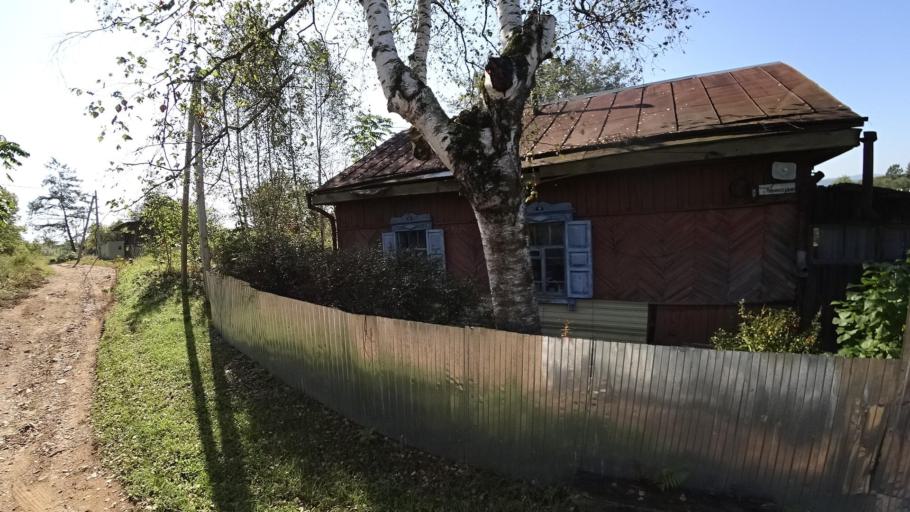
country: RU
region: Jewish Autonomous Oblast
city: Bira
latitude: 49.0062
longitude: 132.4643
